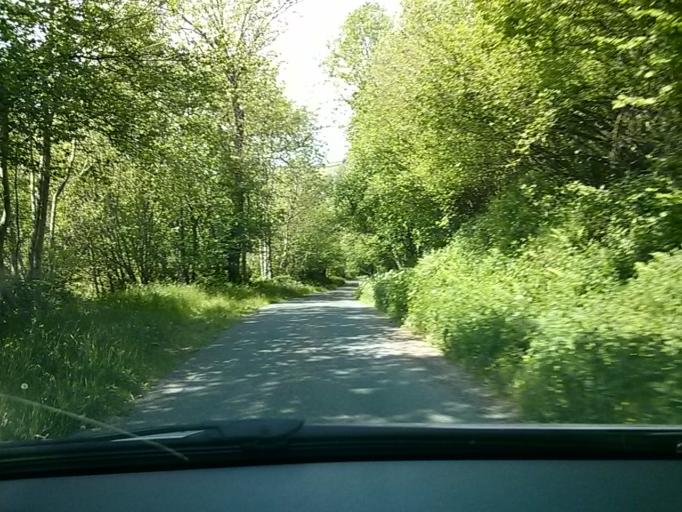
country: FR
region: Rhone-Alpes
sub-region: Departement de la Loire
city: Saint-Chamond
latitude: 45.3955
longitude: 4.5513
